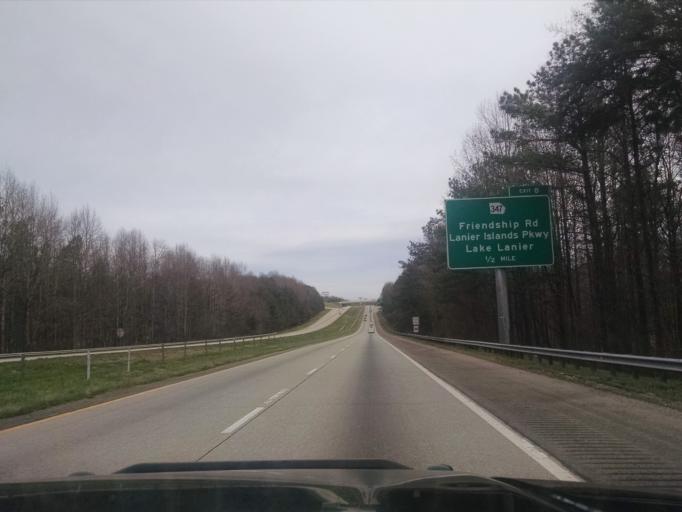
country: US
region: Georgia
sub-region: Gwinnett County
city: Buford
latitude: 34.1325
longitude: -83.9580
